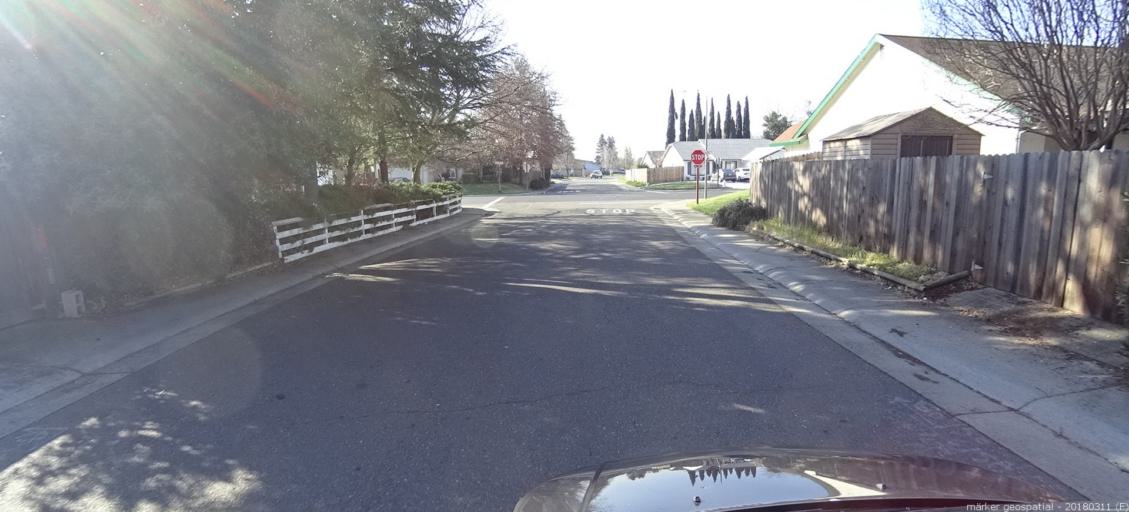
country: US
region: California
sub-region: Sacramento County
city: Florin
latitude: 38.4627
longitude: -121.4033
